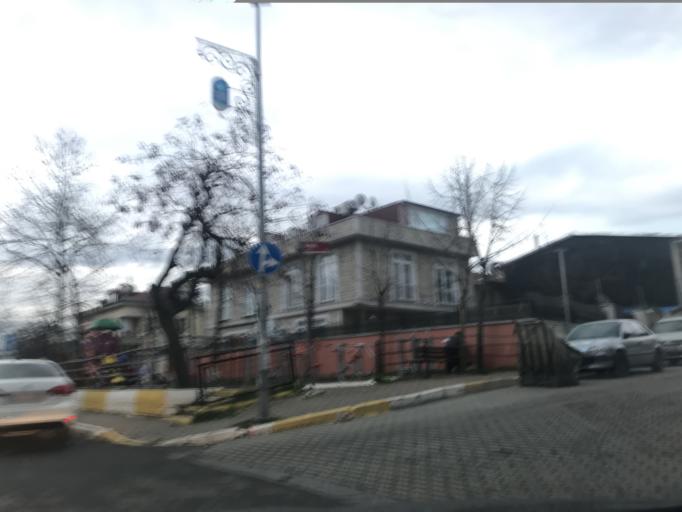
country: TR
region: Istanbul
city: Istanbul
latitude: 41.0431
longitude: 28.9240
